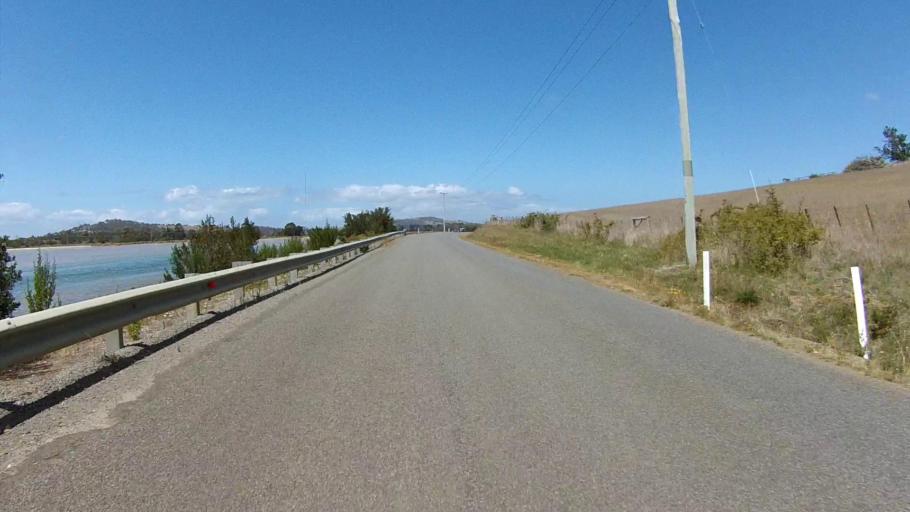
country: AU
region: Tasmania
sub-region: Clarence
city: Lauderdale
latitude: -42.9192
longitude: 147.4778
